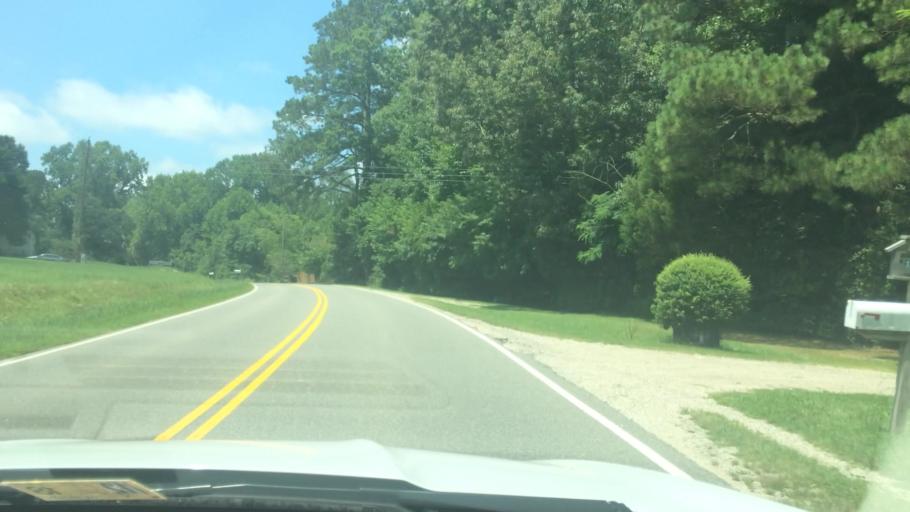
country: US
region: Virginia
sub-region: James City County
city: Williamsburg
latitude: 37.2802
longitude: -76.7934
